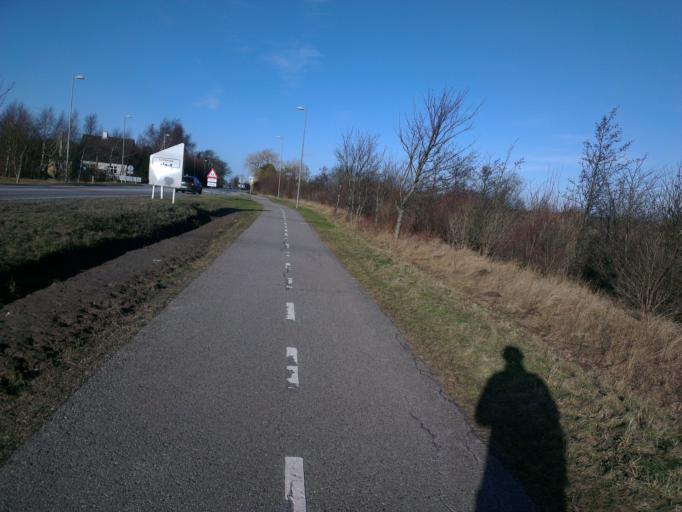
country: DK
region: Capital Region
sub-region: Frederikssund Kommune
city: Skibby
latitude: 55.8018
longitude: 11.9814
